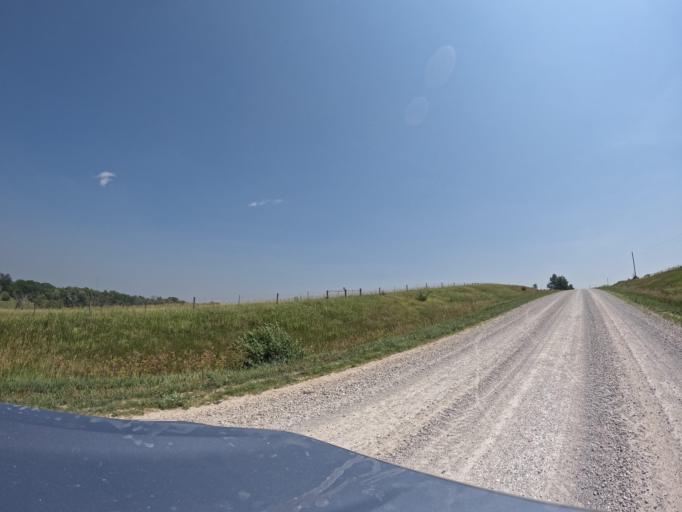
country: US
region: Iowa
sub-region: Keokuk County
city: Sigourney
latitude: 41.3471
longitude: -92.2388
